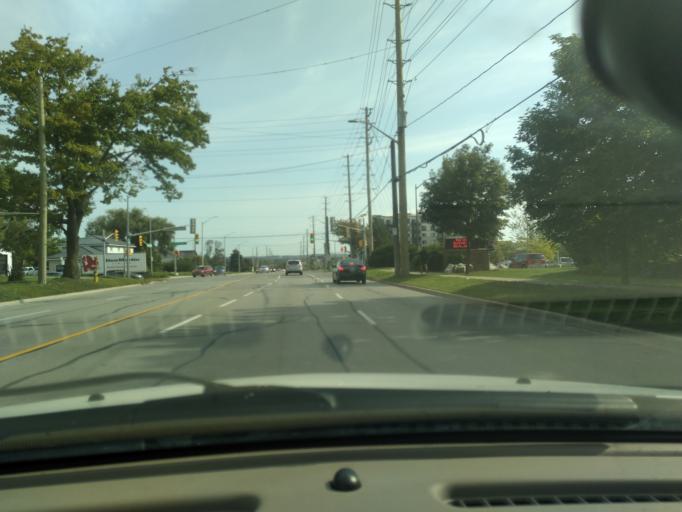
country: CA
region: Ontario
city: Barrie
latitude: 44.4132
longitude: -79.6849
